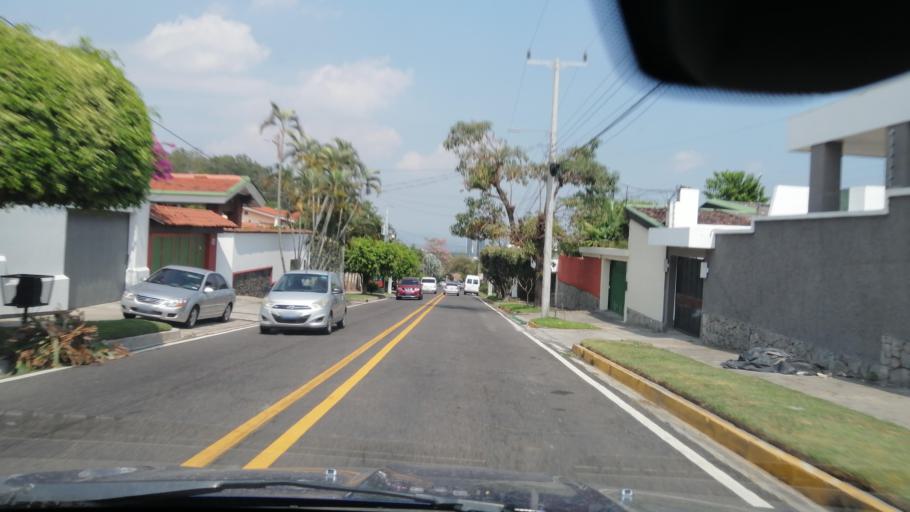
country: SV
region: La Libertad
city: Antiguo Cuscatlan
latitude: 13.6985
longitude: -89.2445
